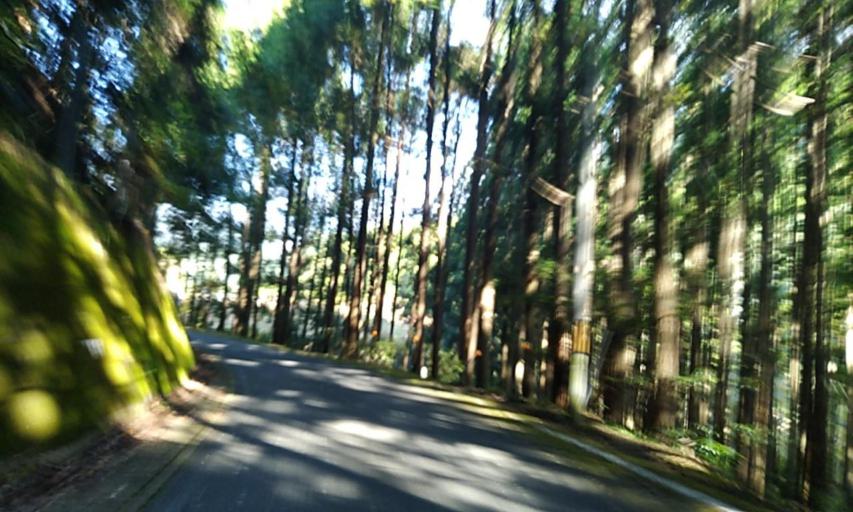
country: JP
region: Wakayama
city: Shingu
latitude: 33.9146
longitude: 135.9904
